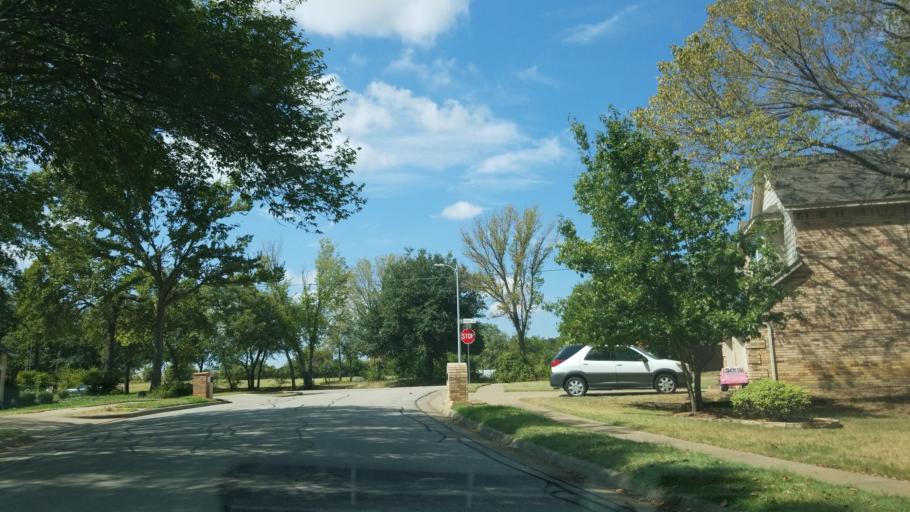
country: US
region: Texas
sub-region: Tarrant County
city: Euless
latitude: 32.8555
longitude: -97.1037
